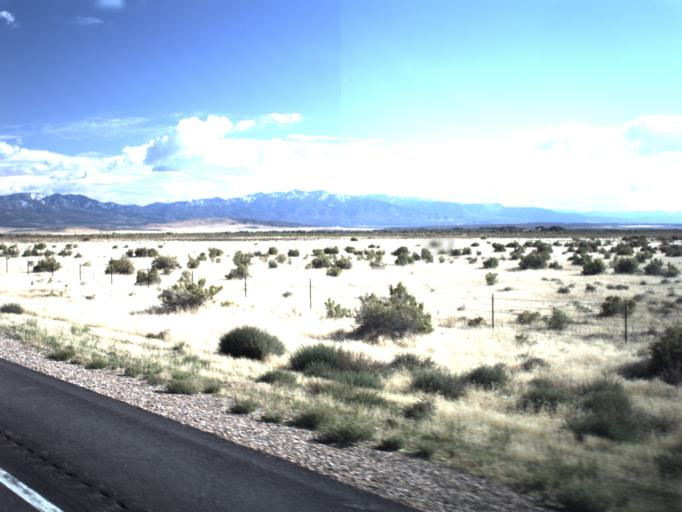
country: US
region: Utah
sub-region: Millard County
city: Fillmore
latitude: 39.1533
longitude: -112.4034
